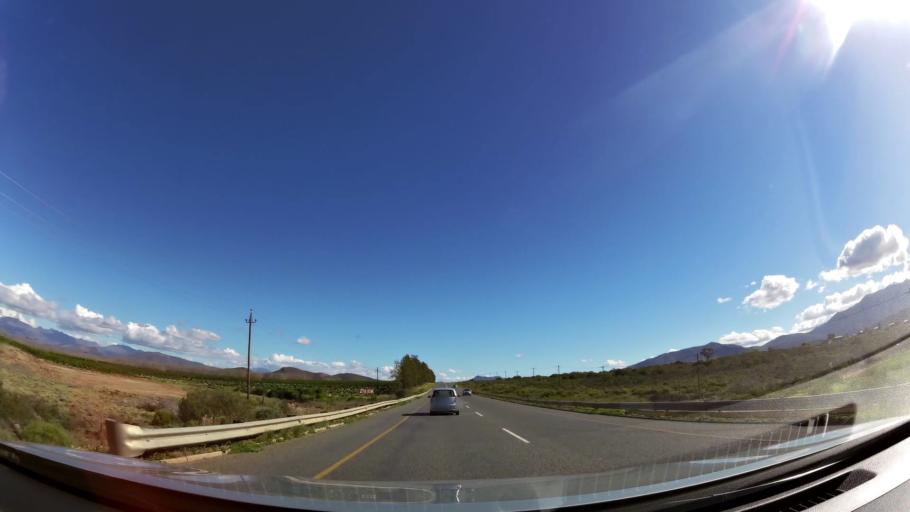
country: ZA
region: Western Cape
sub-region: Cape Winelands District Municipality
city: Ashton
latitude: -33.8143
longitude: 19.9287
